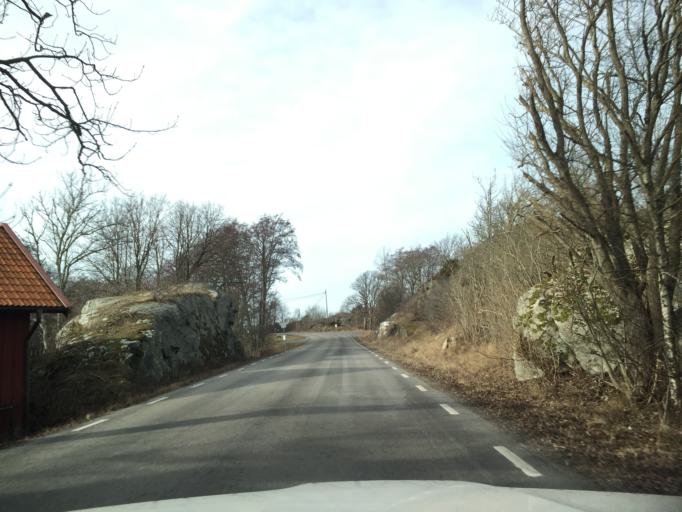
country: SE
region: Vaestra Goetaland
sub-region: Tjorns Kommun
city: Skaerhamn
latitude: 58.0182
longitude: 11.5288
